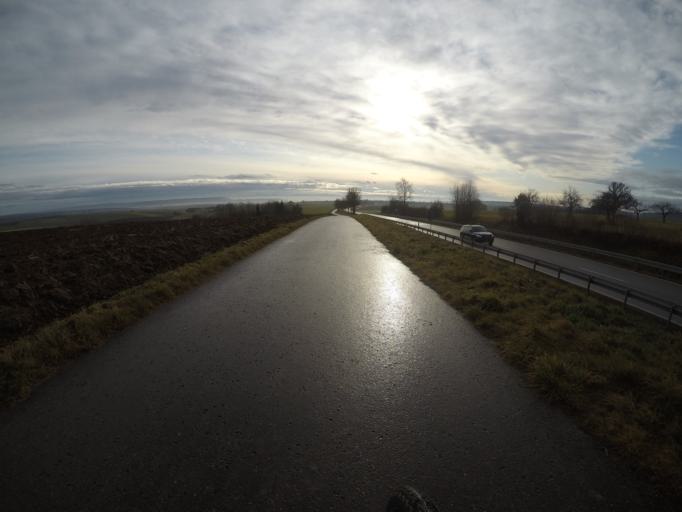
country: DE
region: Baden-Wuerttemberg
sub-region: Regierungsbezirk Stuttgart
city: Deckenpfronn
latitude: 48.6405
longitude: 8.8243
